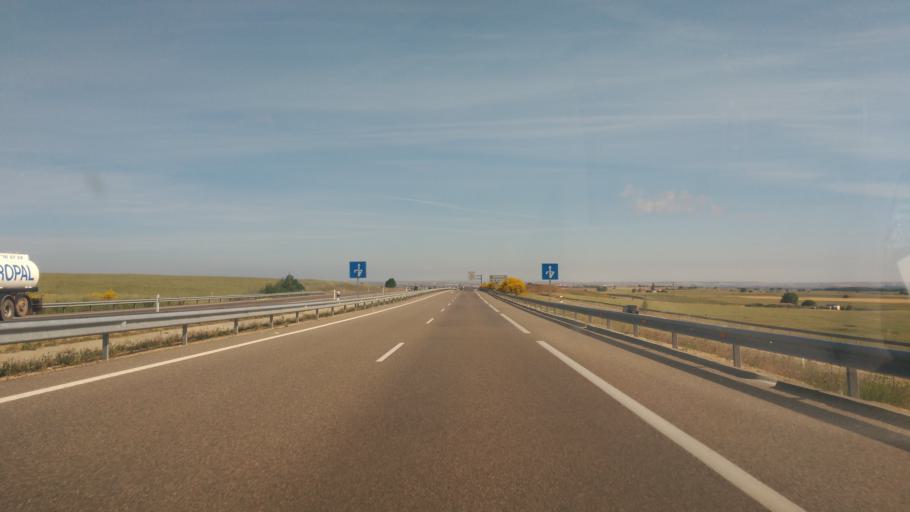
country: ES
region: Castille and Leon
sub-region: Provincia de Zamora
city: Cazurra
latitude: 41.4108
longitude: -5.7196
